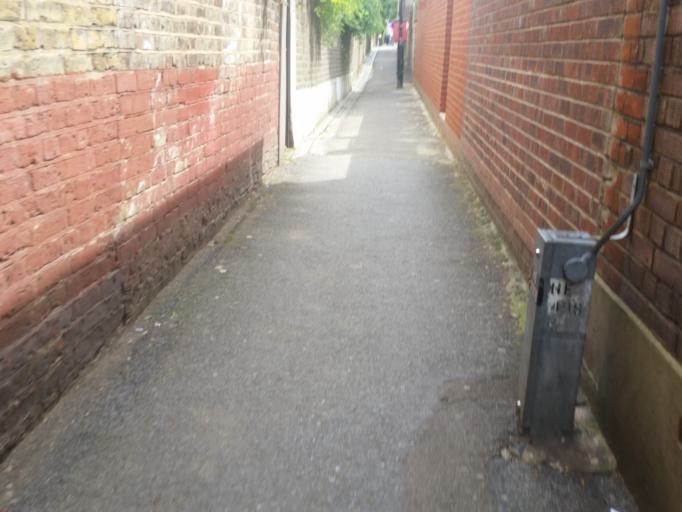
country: GB
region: England
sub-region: Greater London
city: Harringay
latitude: 51.5877
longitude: -0.1054
